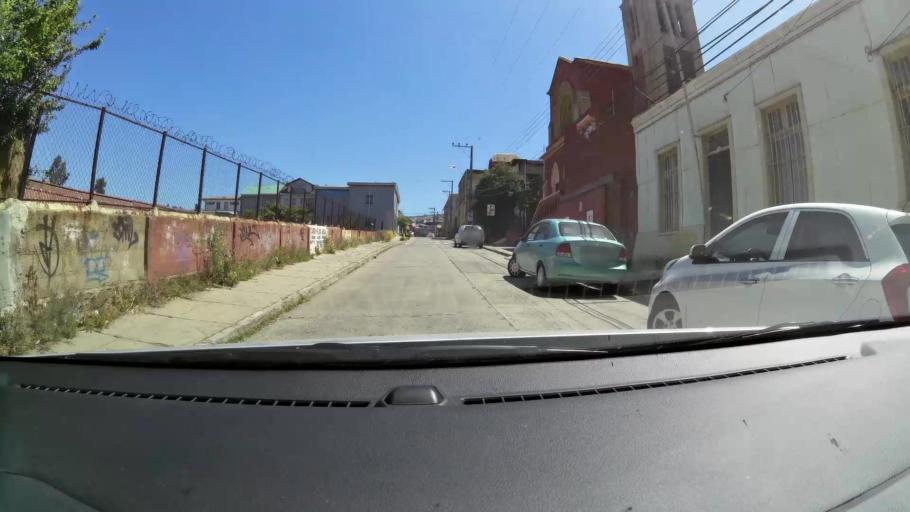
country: CL
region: Valparaiso
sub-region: Provincia de Valparaiso
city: Valparaiso
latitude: -33.0317
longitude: -71.6350
